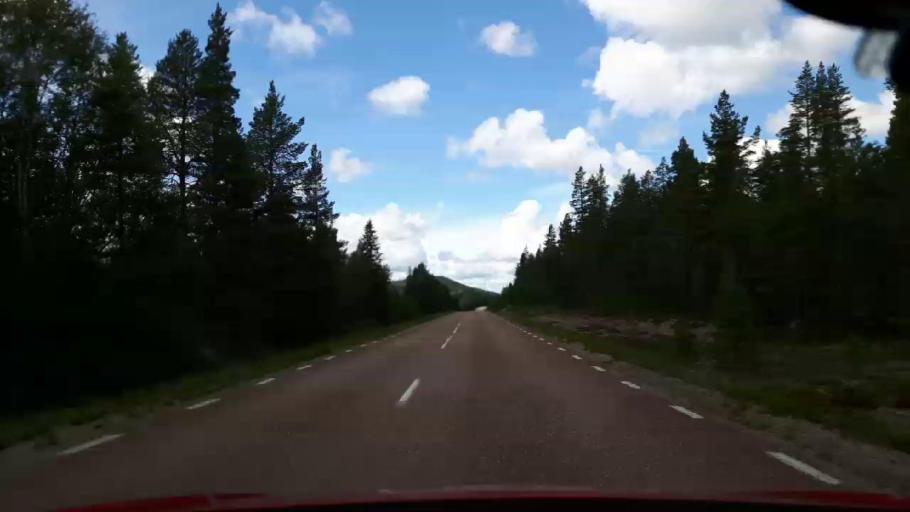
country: SE
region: Dalarna
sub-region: Alvdalens Kommun
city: AElvdalen
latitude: 61.7980
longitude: 13.6989
